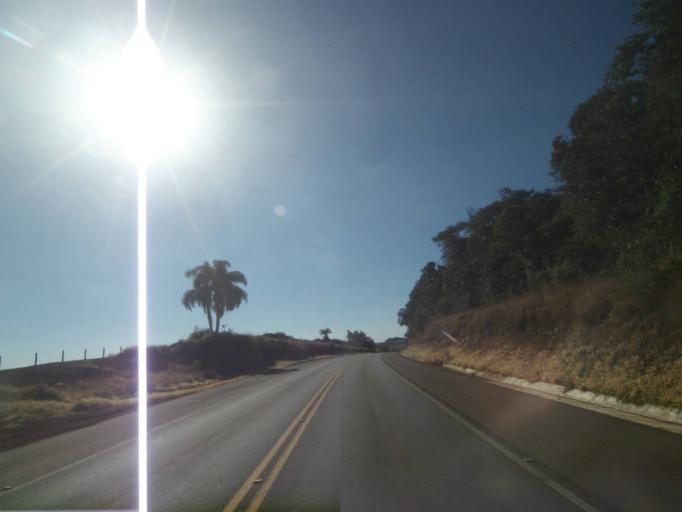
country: BR
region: Parana
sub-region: Tibagi
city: Tibagi
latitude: -24.7104
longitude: -50.4499
